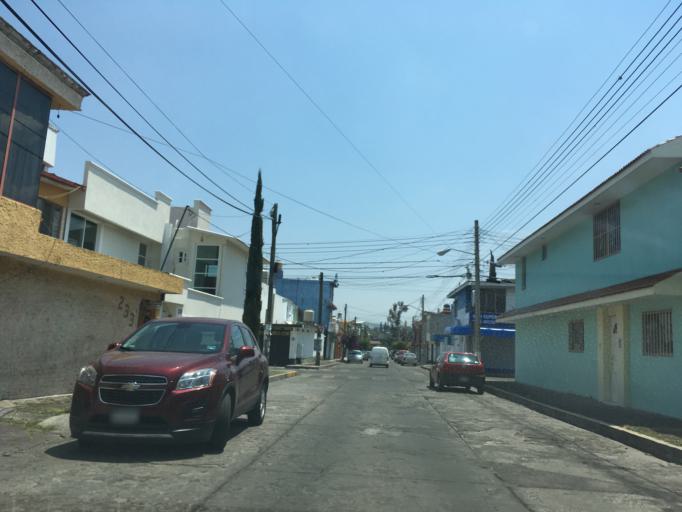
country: MX
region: Michoacan
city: Morelia
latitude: 19.6845
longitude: -101.2149
